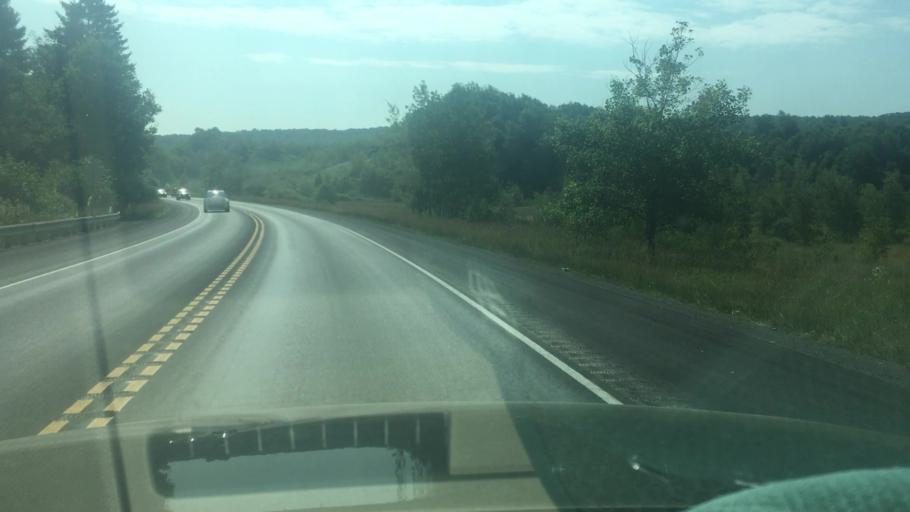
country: US
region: Pennsylvania
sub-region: Northumberland County
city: Mount Carmel
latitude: 40.7699
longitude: -76.4395
